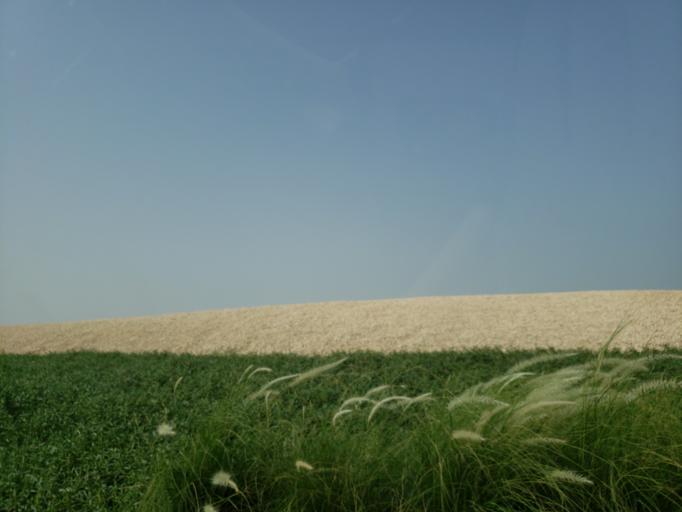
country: AE
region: Ajman
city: Ajman
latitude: 25.4356
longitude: 55.4671
